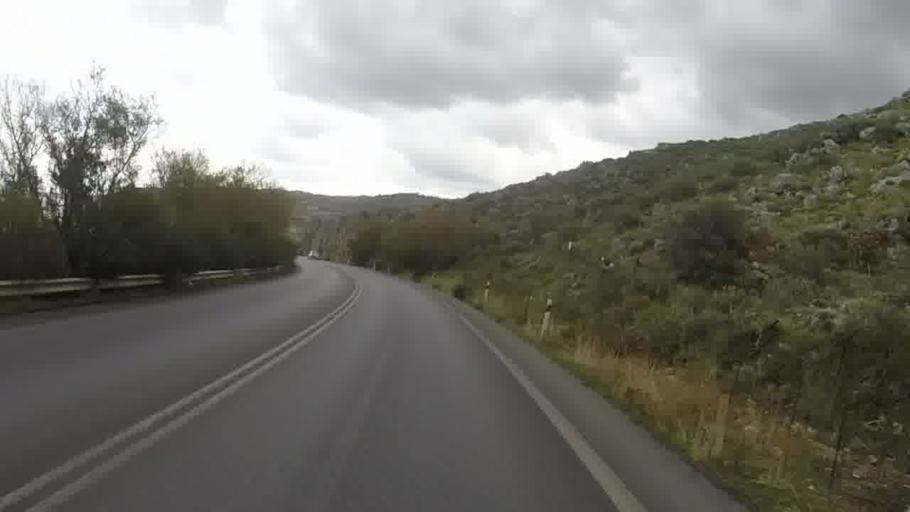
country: GR
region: Crete
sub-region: Nomos Rethymnis
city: Atsipopoulon
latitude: 35.3601
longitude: 24.3834
